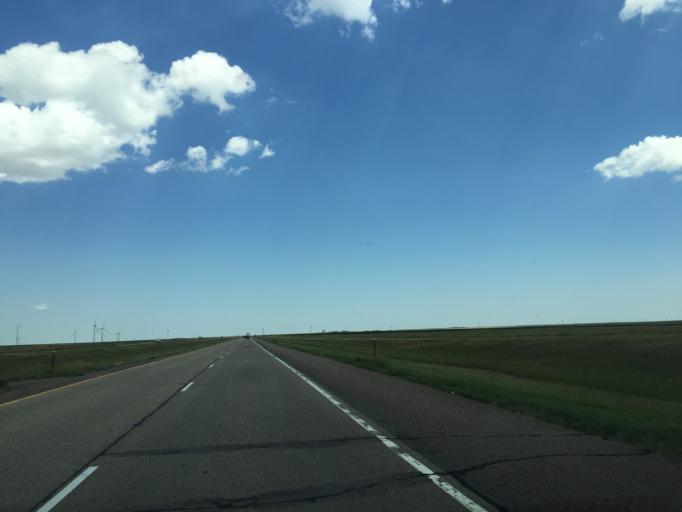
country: US
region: Colorado
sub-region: Lincoln County
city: Hugo
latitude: 39.2781
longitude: -103.4323
